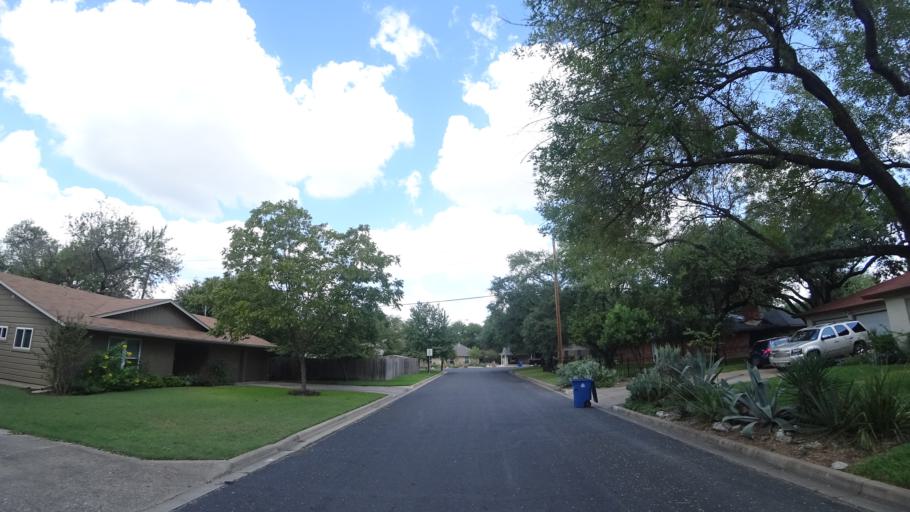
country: US
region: Texas
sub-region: Travis County
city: Austin
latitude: 30.3591
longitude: -97.7276
